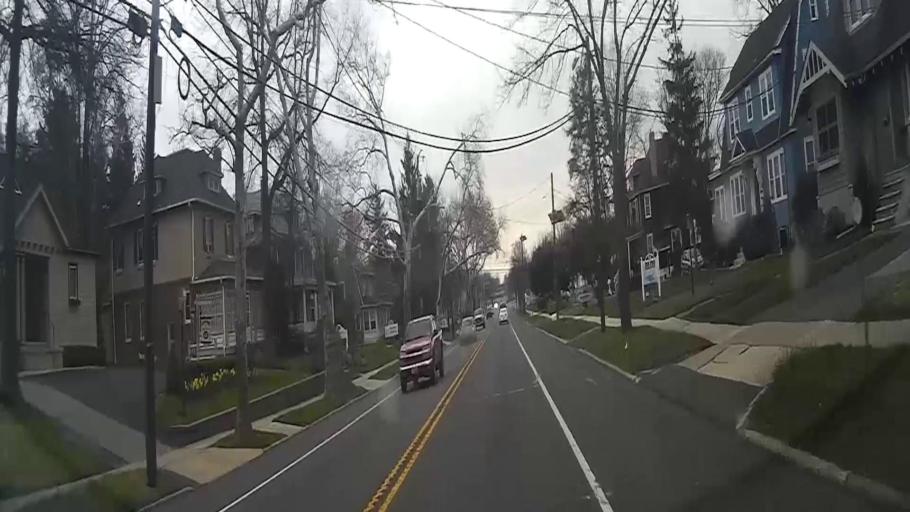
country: US
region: New Jersey
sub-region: Camden County
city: Haddon Heights
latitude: 39.8795
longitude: -75.0530
